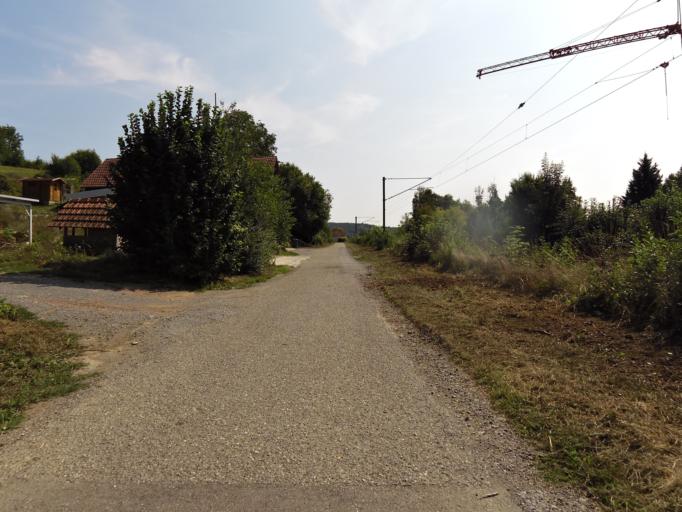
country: DE
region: Baden-Wuerttemberg
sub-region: Karlsruhe Region
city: Waibstadt
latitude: 49.3059
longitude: 8.9042
